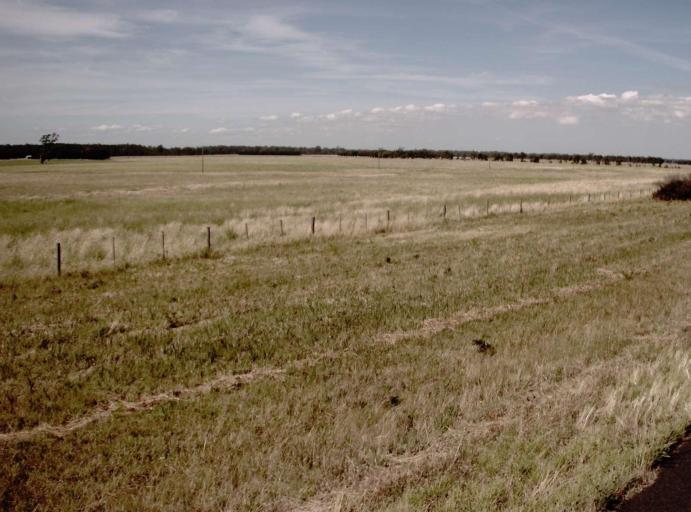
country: AU
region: Victoria
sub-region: Wellington
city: Heyfield
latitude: -38.1622
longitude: 146.8644
